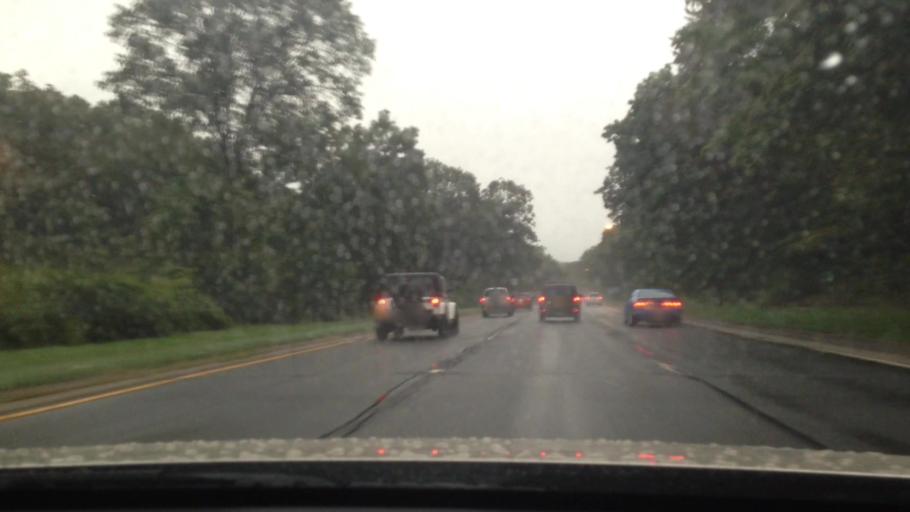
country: US
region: New York
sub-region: Suffolk County
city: North Babylon
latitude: 40.7331
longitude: -73.3066
